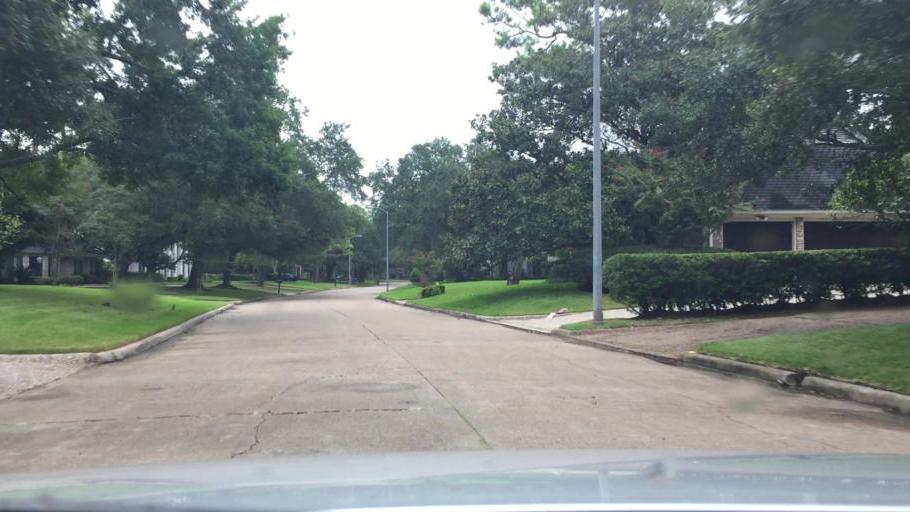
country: US
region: Texas
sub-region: Harris County
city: Hunters Creek Village
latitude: 29.7675
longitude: -95.5055
